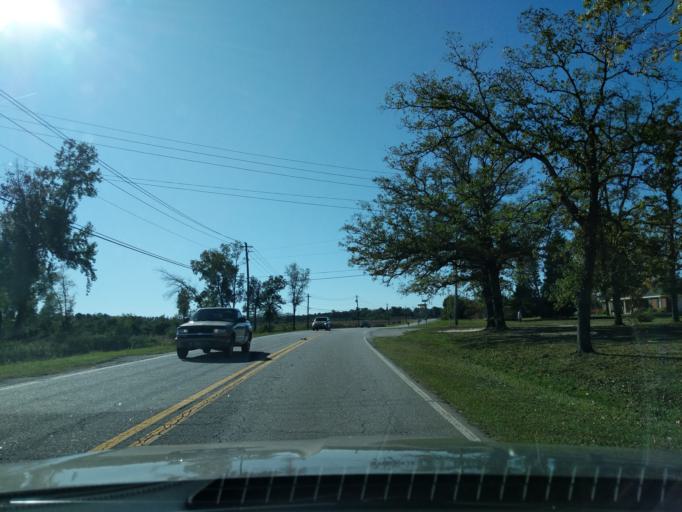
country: US
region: Georgia
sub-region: Columbia County
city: Grovetown
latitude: 33.4668
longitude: -82.1611
